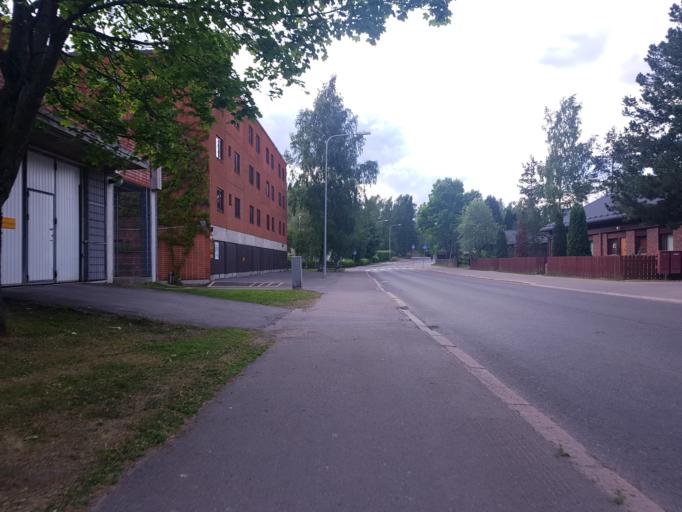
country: FI
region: Uusimaa
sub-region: Helsinki
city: Vantaa
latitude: 60.2480
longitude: 24.9905
